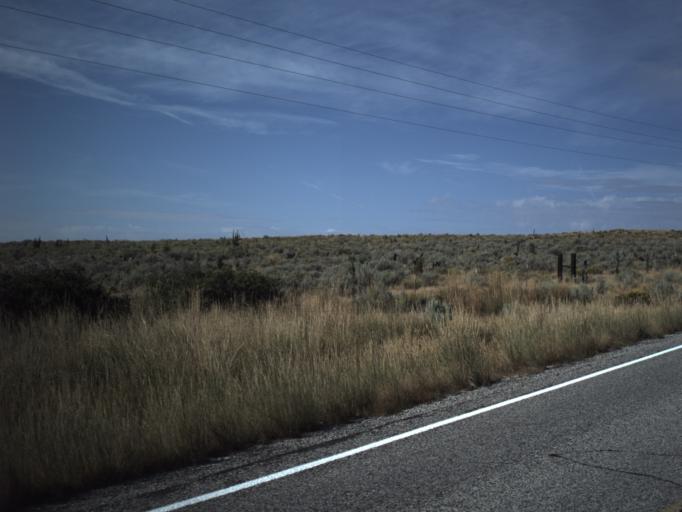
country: US
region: Idaho
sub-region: Cassia County
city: Burley
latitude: 41.8174
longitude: -113.2532
